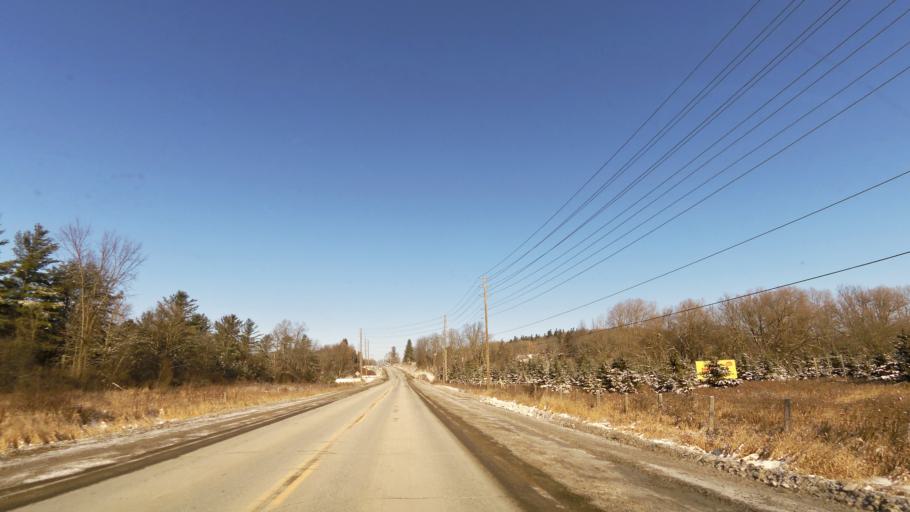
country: CA
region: Ontario
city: Quinte West
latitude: 44.1980
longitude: -77.8178
